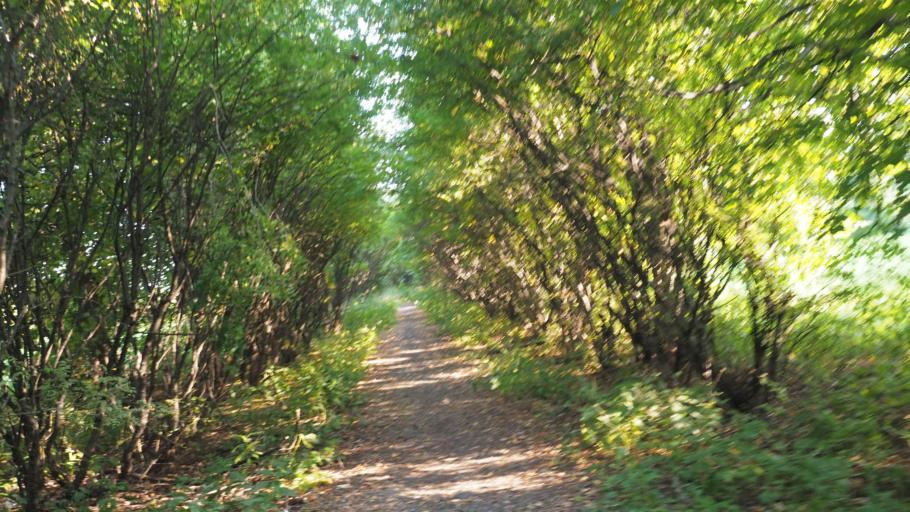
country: RU
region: Moscow
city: Orekhovo-Borisovo Severnoye
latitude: 55.6199
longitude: 37.6909
